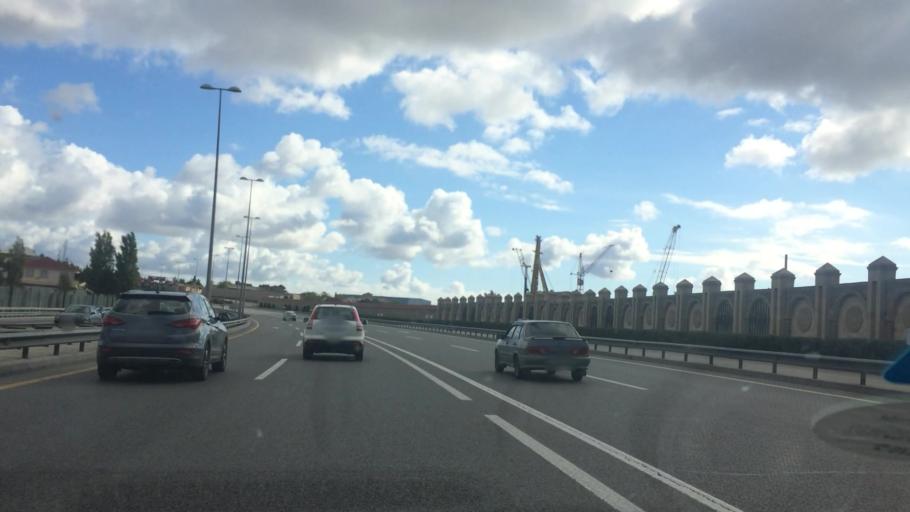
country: AZ
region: Baki
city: Ramana
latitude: 40.4383
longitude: 49.9779
